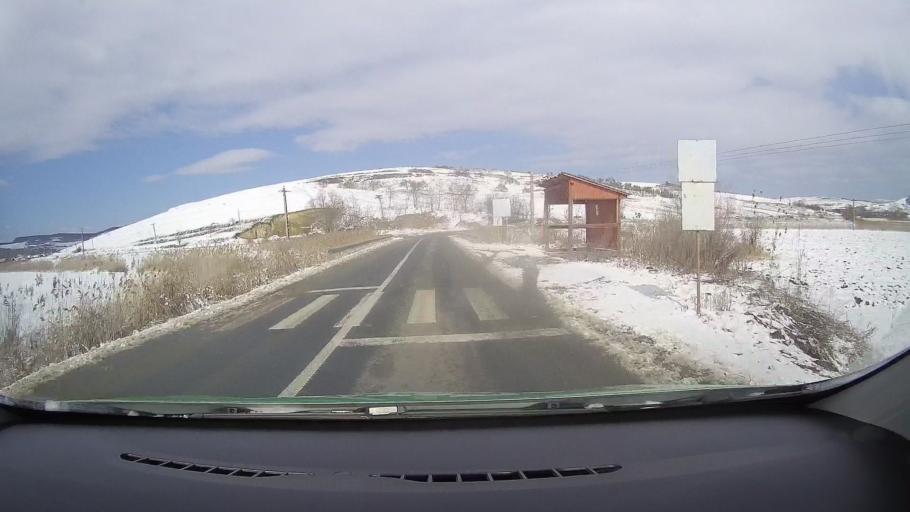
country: RO
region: Sibiu
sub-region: Comuna Altina
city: Altina
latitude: 45.9773
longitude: 24.4657
